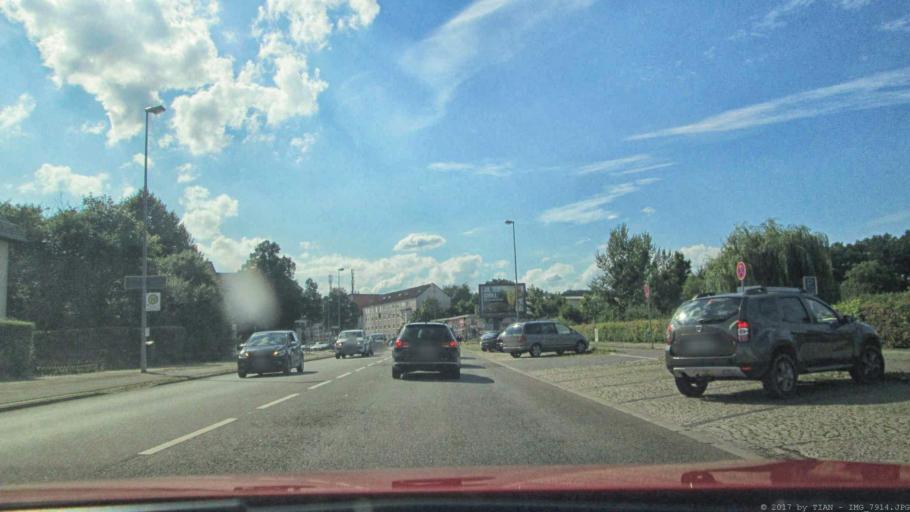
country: DE
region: Lower Saxony
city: Wolfsburg
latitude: 52.4210
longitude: 10.7679
